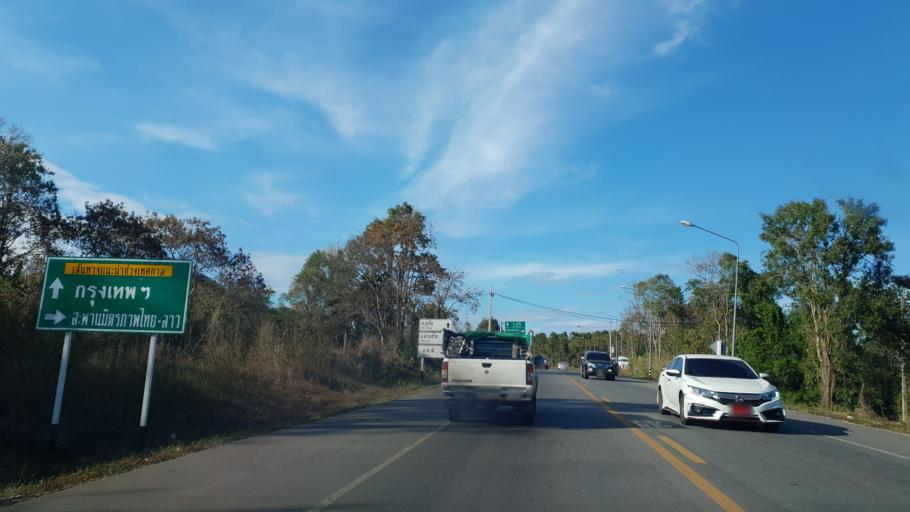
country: TH
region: Loei
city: Phu Ruea
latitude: 17.4441
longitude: 101.4674
